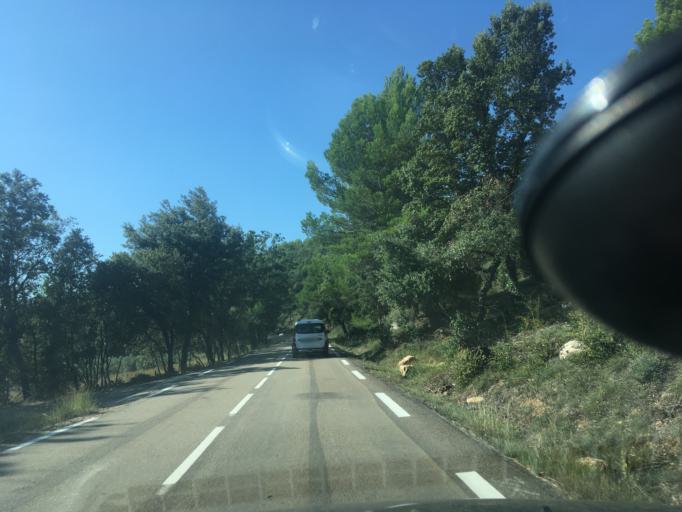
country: FR
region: Provence-Alpes-Cote d'Azur
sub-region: Departement du Var
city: Regusse
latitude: 43.6135
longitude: 6.0692
